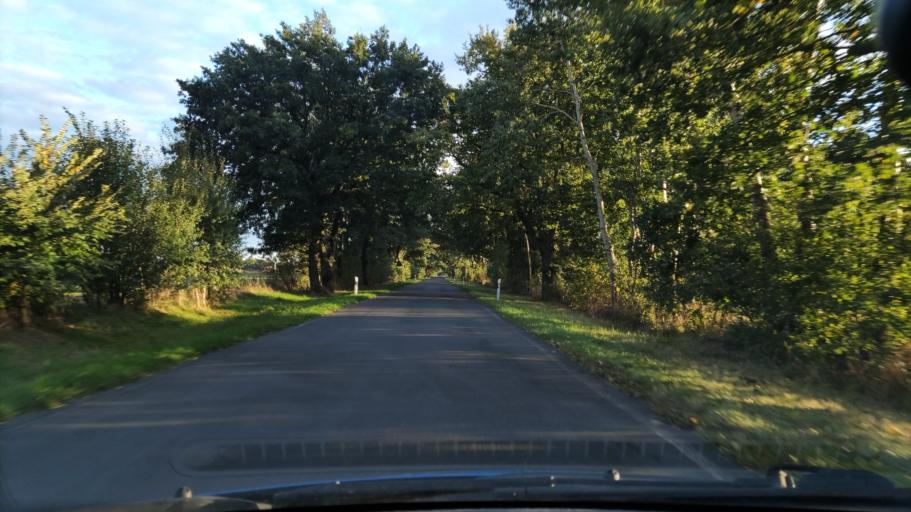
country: DE
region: Lower Saxony
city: Neu Darchau
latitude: 53.3516
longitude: 10.8632
